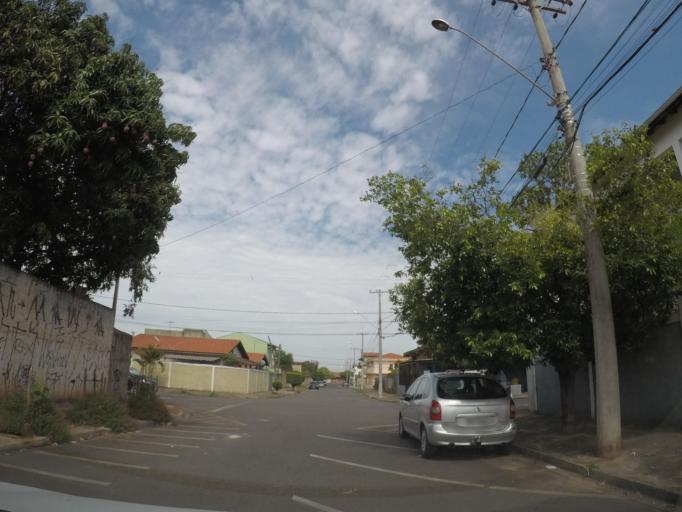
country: BR
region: Sao Paulo
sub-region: Hortolandia
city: Hortolandia
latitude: -22.8322
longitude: -47.1871
